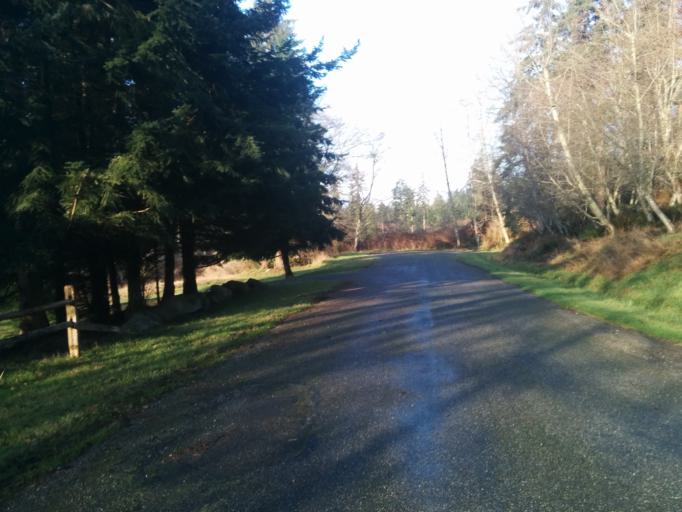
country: US
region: Washington
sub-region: Island County
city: Freeland
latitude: 48.0506
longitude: -122.4976
